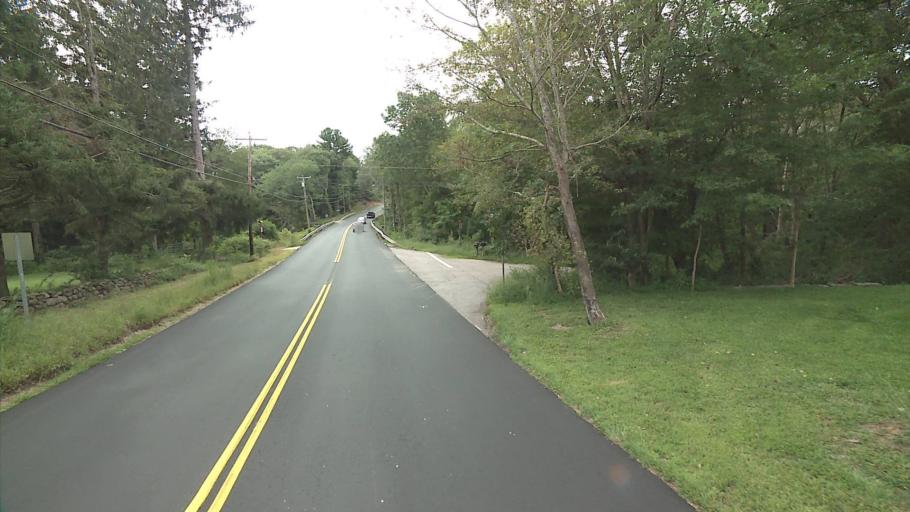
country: US
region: Connecticut
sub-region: New London County
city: Colchester
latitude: 41.5968
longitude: -72.3415
